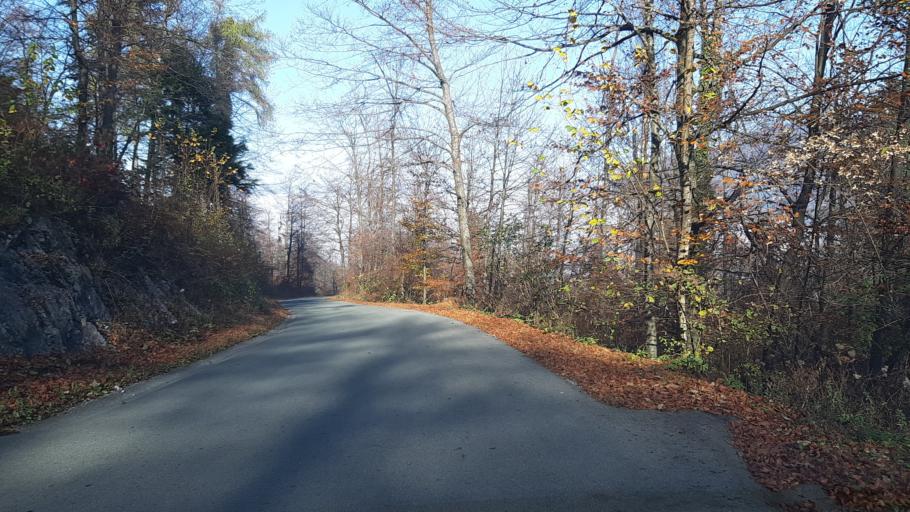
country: SI
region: Borovnica
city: Borovnica
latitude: 45.9030
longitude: 14.3637
